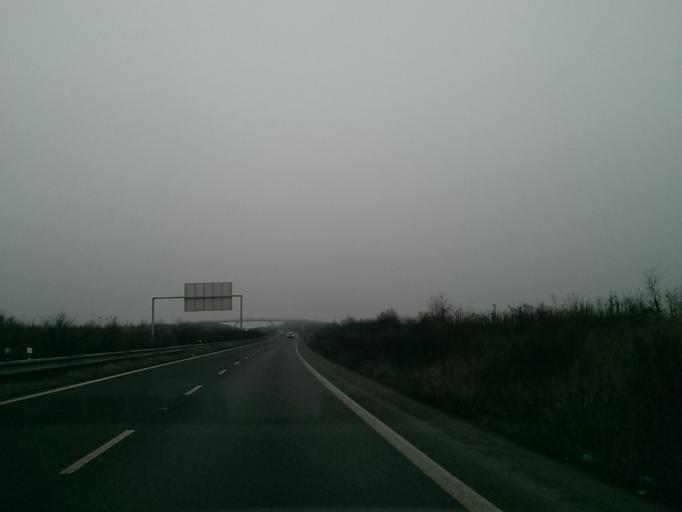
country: CZ
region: Olomoucky
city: Horka nad Moravou
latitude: 49.6030
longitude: 17.2115
